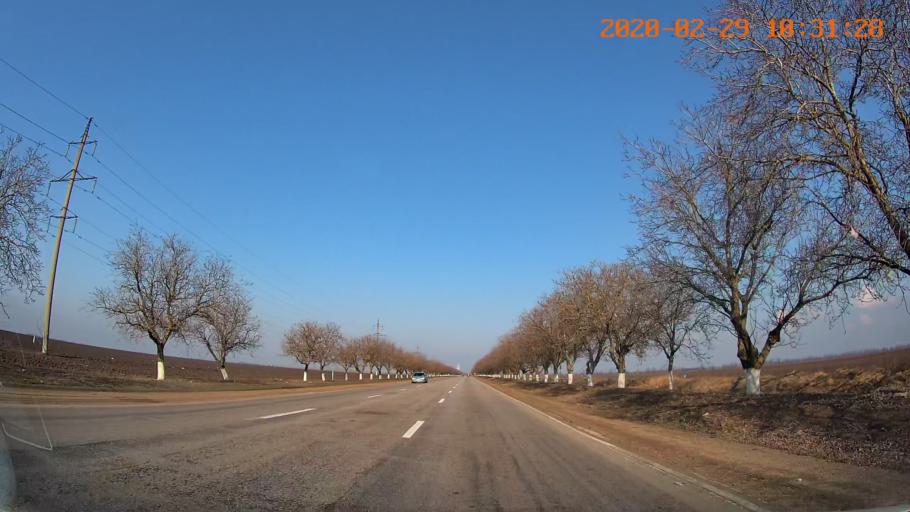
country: MD
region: Telenesti
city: Tiraspolul Nou
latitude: 46.9487
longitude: 29.5637
